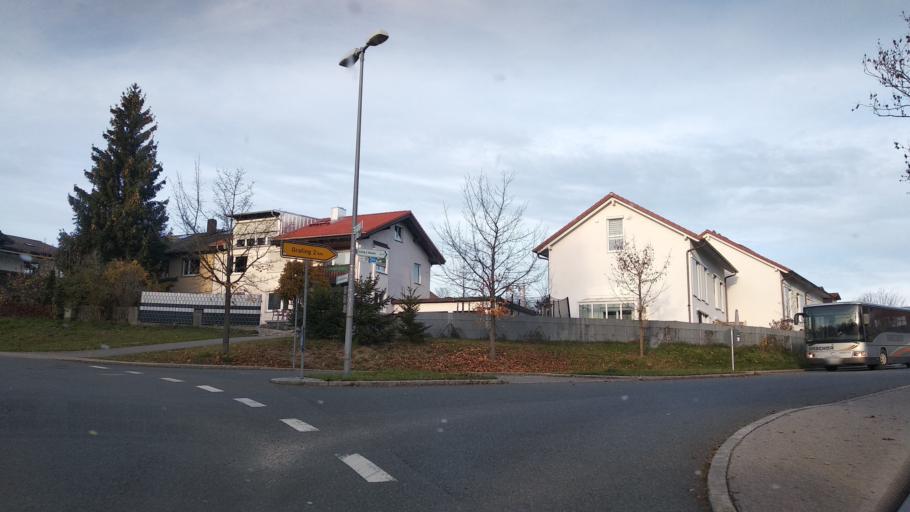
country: DE
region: Bavaria
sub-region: Upper Bavaria
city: Grafing bei Munchen
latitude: 48.0411
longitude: 11.9431
